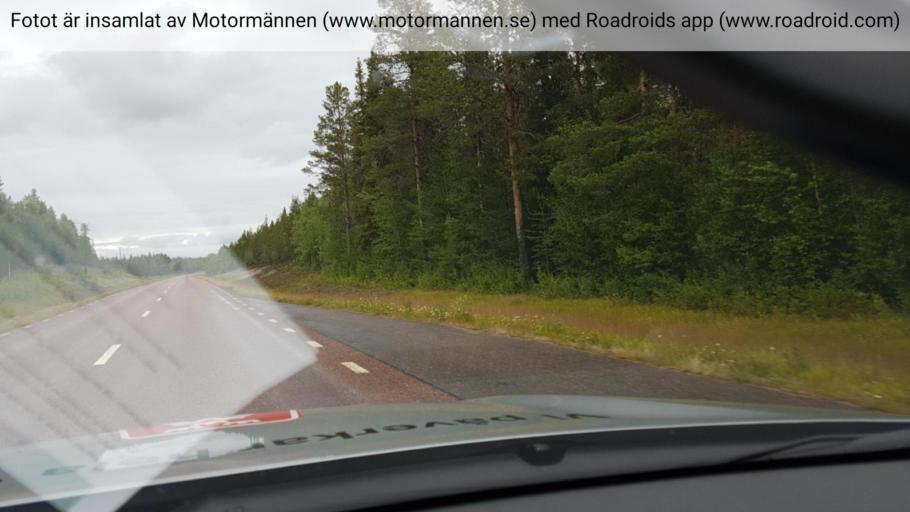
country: SE
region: Norrbotten
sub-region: Pajala Kommun
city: Pajala
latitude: 67.1253
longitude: 22.6062
